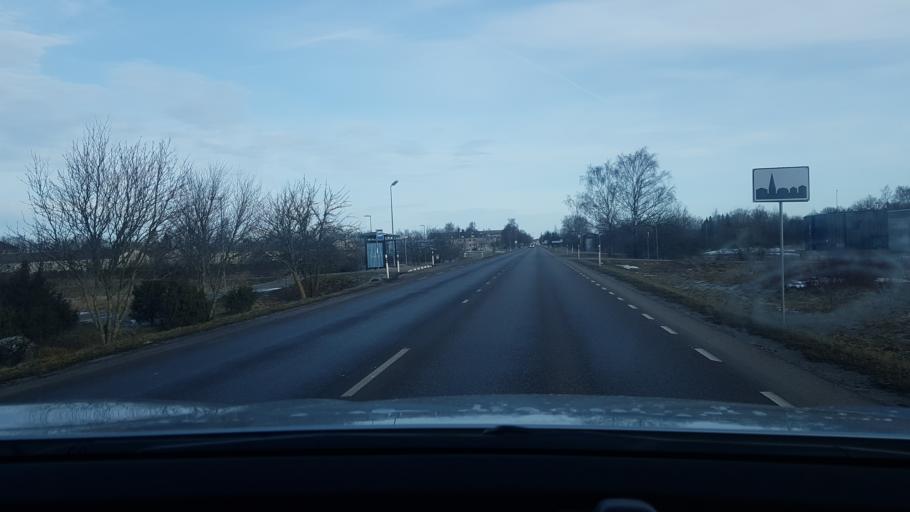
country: EE
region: Saare
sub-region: Kuressaare linn
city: Kuressaare
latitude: 58.2490
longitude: 22.5070
